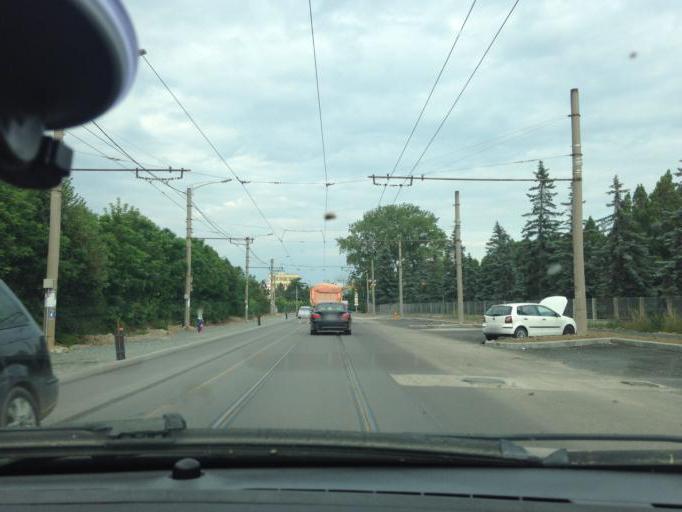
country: RO
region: Cluj
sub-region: Municipiul Cluj-Napoca
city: Cluj-Napoca
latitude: 46.7956
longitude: 23.6256
